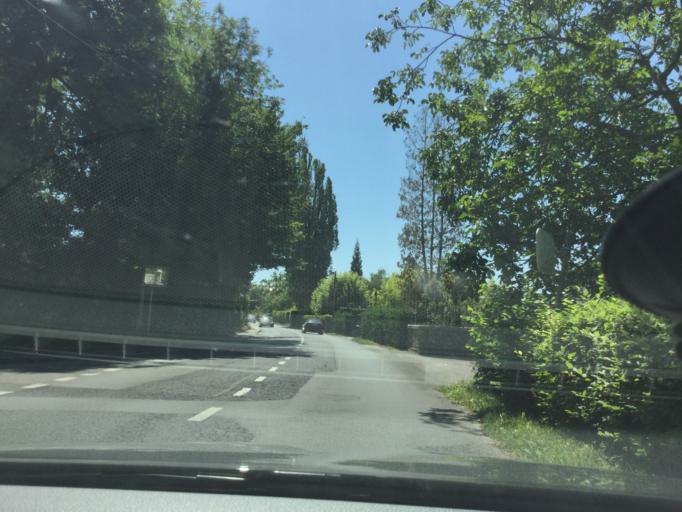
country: CH
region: Geneva
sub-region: Geneva
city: Anieres
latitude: 46.2702
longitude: 6.2185
